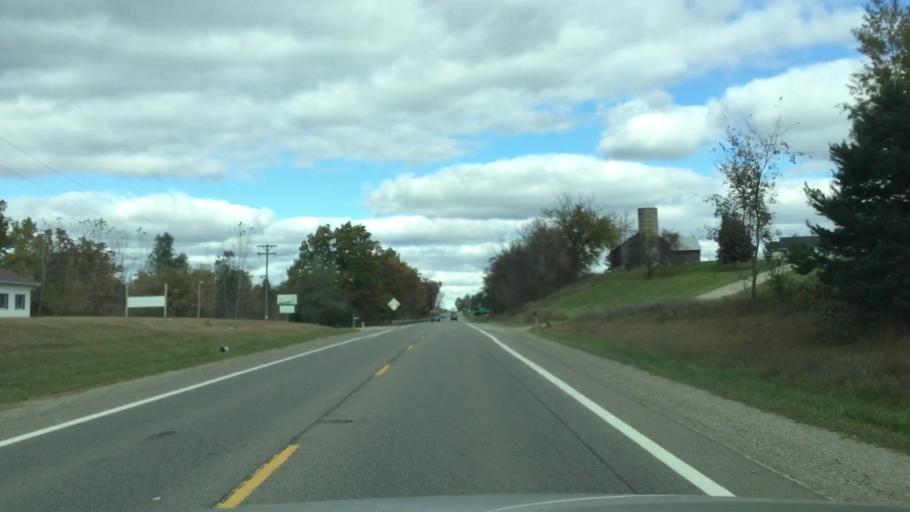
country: US
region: Michigan
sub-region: Lapeer County
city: Barnes Lake-Millers Lake
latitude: 43.1828
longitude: -83.3123
